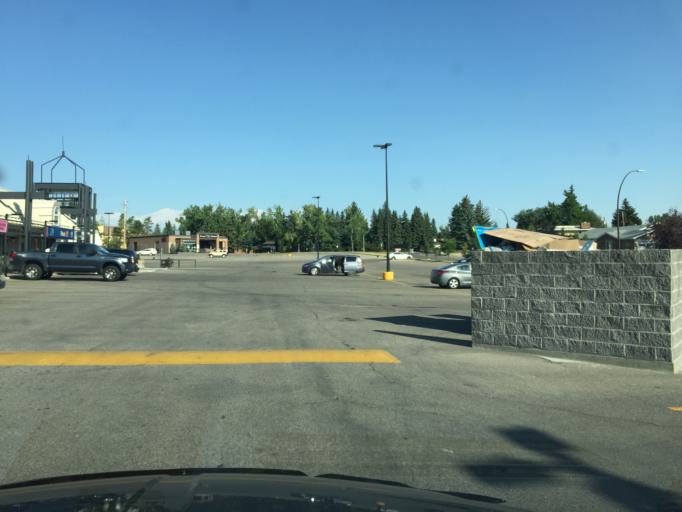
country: CA
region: Alberta
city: Calgary
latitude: 50.9425
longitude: -114.0466
